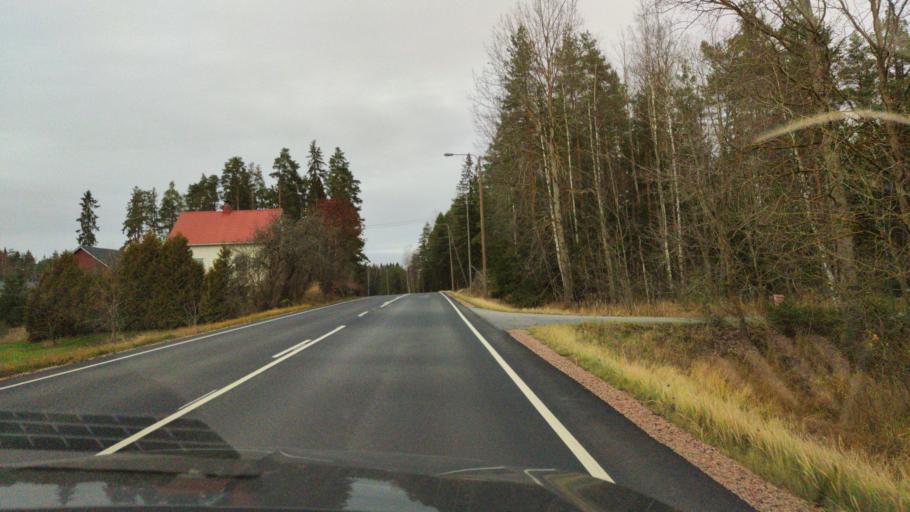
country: FI
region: Varsinais-Suomi
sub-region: Turku
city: Vahto
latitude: 60.6510
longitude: 22.4282
